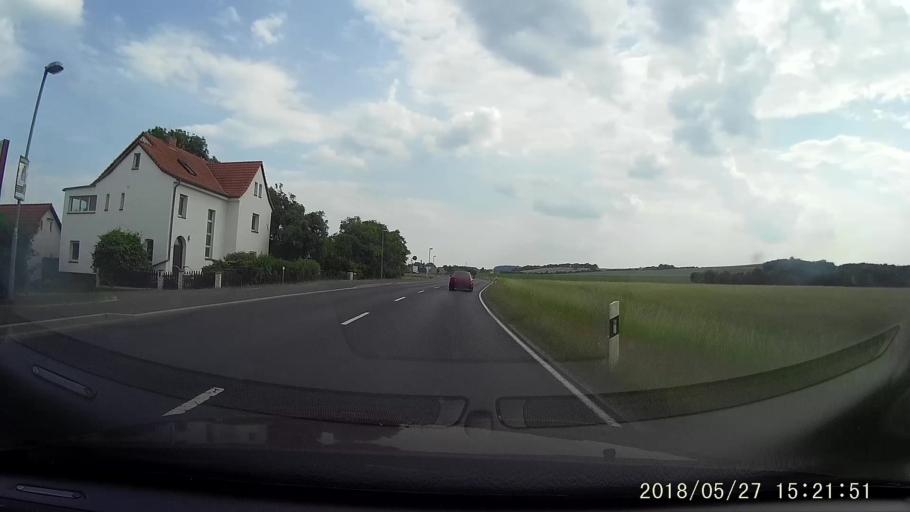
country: DE
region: Saxony
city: Kodersdorf
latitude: 51.2379
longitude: 14.8896
